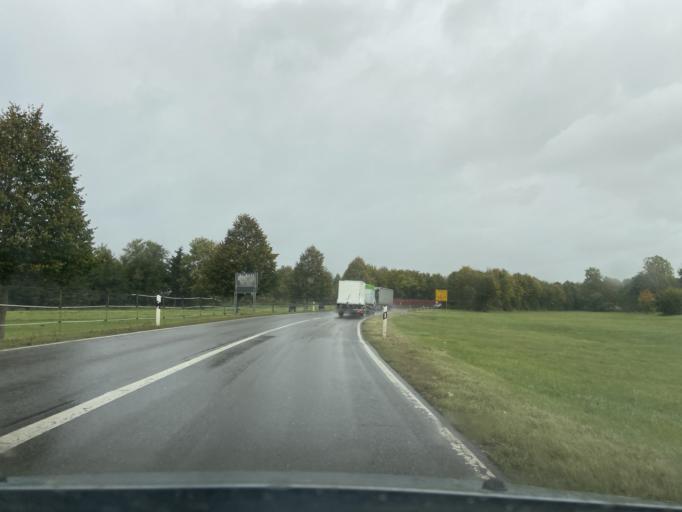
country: DE
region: Baden-Wuerttemberg
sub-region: Tuebingen Region
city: Ennetach
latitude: 48.0491
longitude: 9.3218
